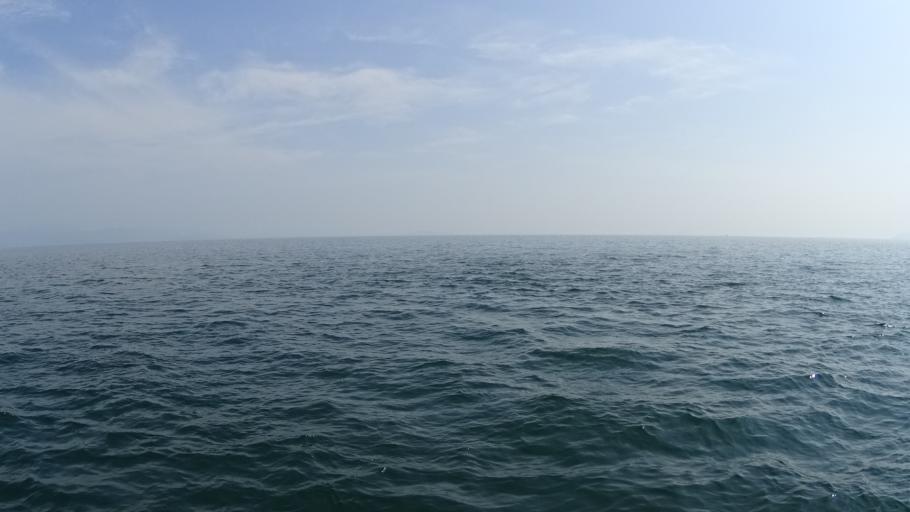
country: JP
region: Shiga Prefecture
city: Nagahama
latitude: 35.4195
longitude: 136.1436
